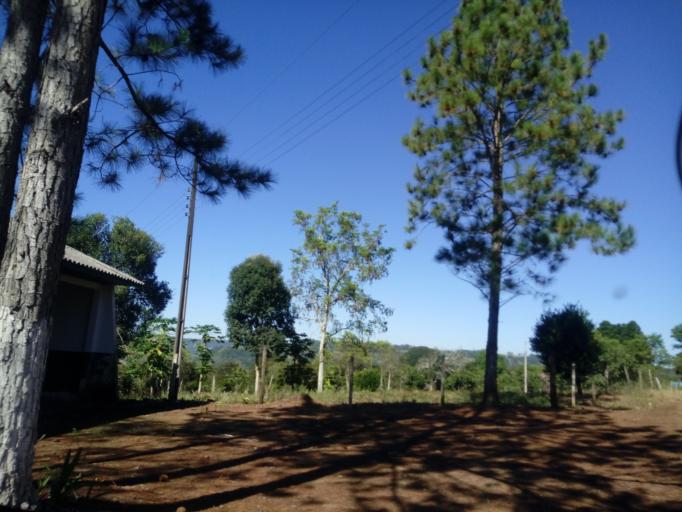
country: BR
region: Santa Catarina
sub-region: Chapeco
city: Chapeco
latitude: -27.1958
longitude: -52.7624
